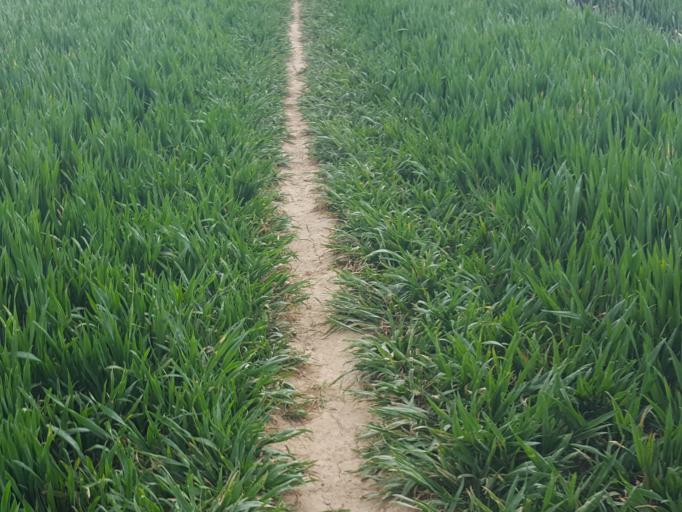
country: GB
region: England
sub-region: Essex
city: Frinton-on-Sea
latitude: 51.8502
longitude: 1.2197
